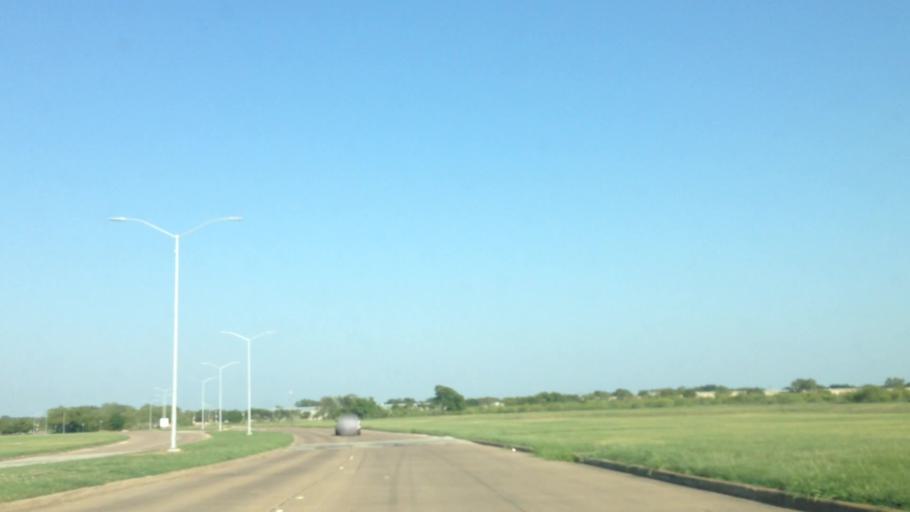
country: US
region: Texas
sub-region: Tarrant County
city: Haltom City
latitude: 32.8101
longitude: -97.3048
